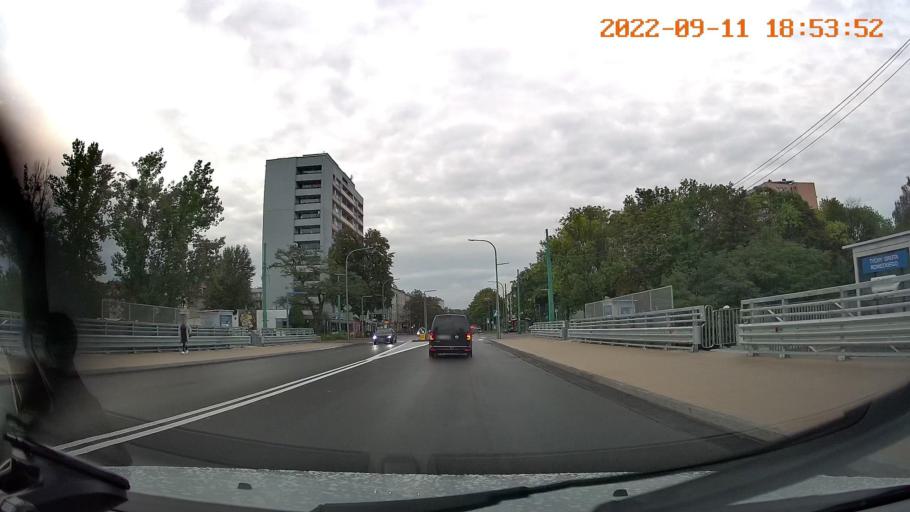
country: PL
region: Silesian Voivodeship
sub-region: Tychy
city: Tychy
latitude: 50.1135
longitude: 18.9870
